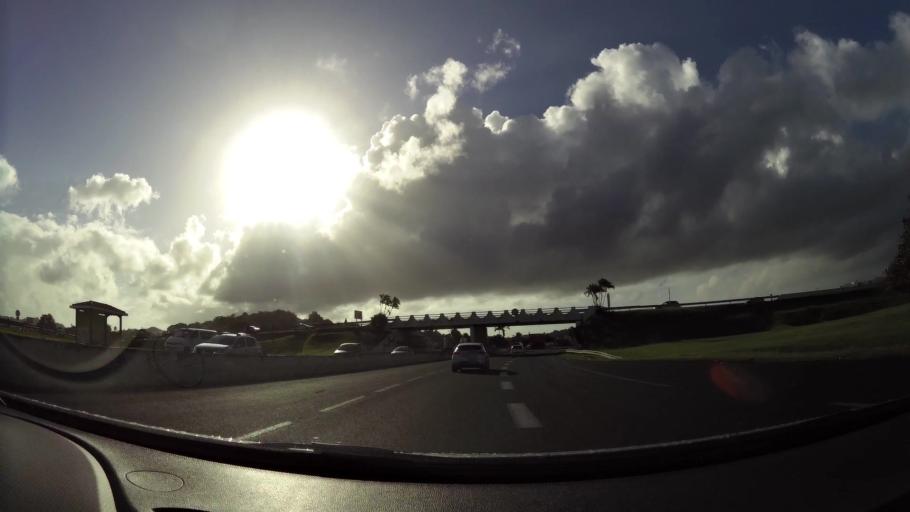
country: MQ
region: Martinique
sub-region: Martinique
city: Ducos
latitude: 14.5944
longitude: -60.9842
